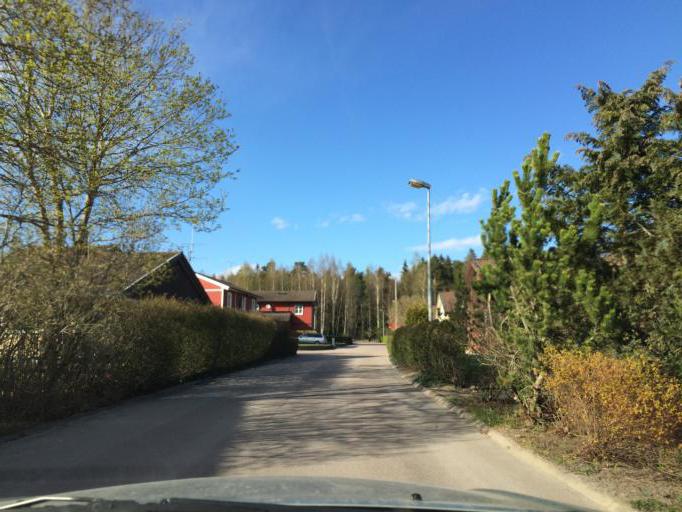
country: SE
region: Vaestmanland
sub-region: Vasteras
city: Hokasen
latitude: 59.6556
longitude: 16.5510
